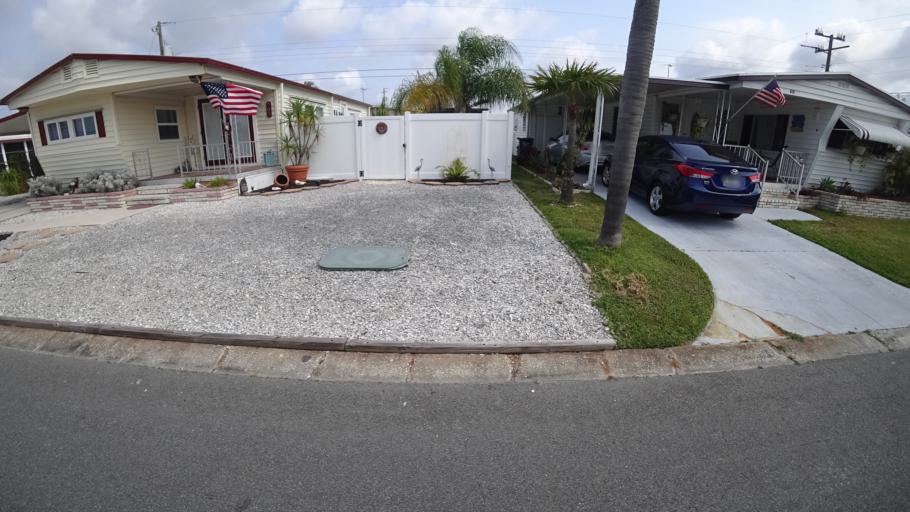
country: US
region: Florida
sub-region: Manatee County
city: South Bradenton
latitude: 27.4498
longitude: -82.5694
